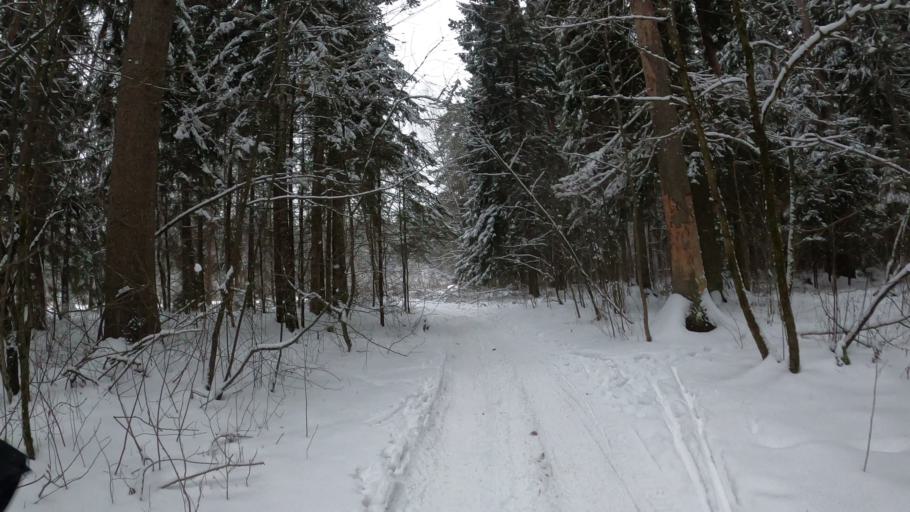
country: RU
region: Moskovskaya
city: Firsanovka
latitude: 55.9295
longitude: 37.2206
